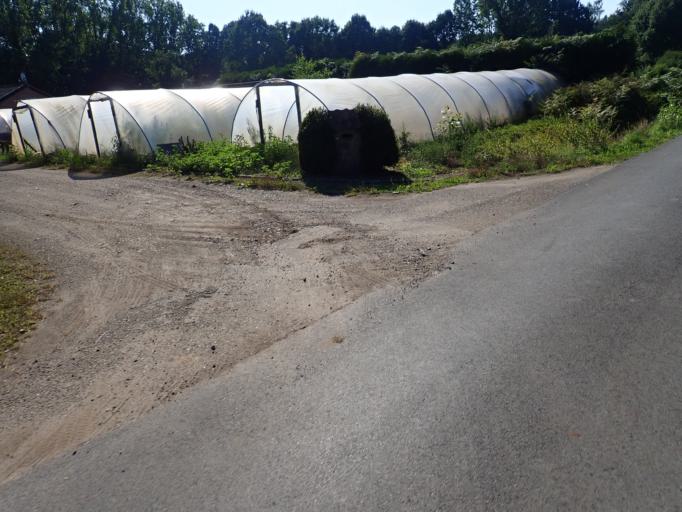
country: BE
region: Flanders
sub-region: Provincie Antwerpen
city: Herselt
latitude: 51.0506
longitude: 4.9099
